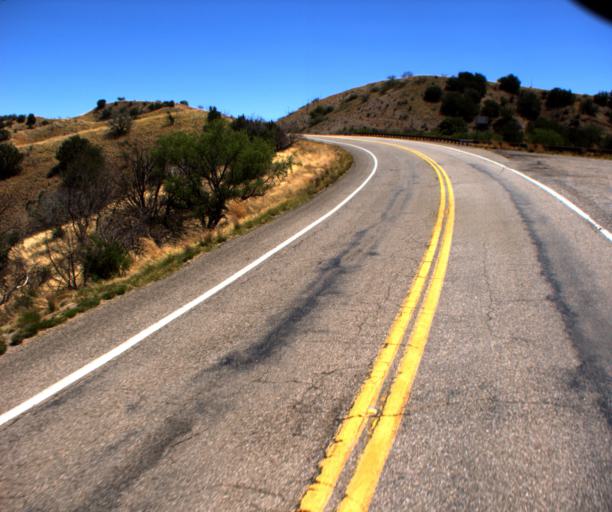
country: US
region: Arizona
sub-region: Pima County
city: Corona de Tucson
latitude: 31.8242
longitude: -110.7142
